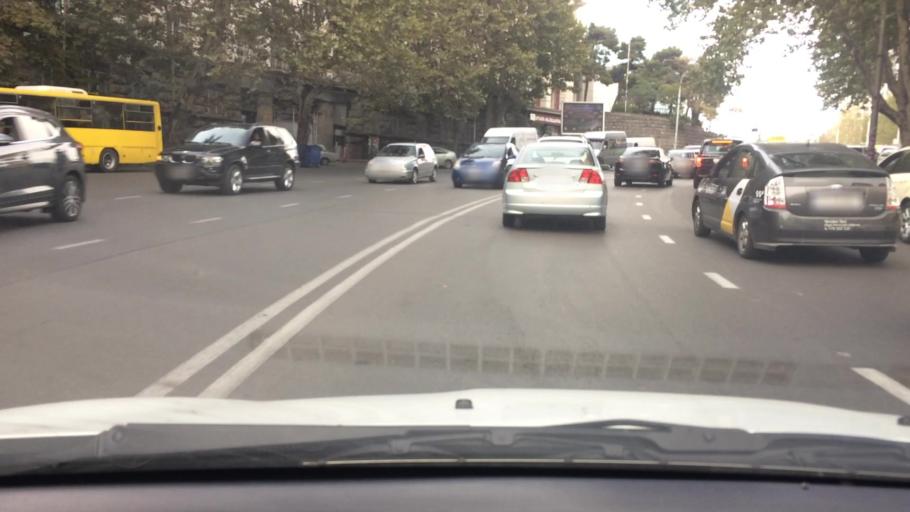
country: GE
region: T'bilisi
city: Tbilisi
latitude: 41.7159
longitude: 44.7788
